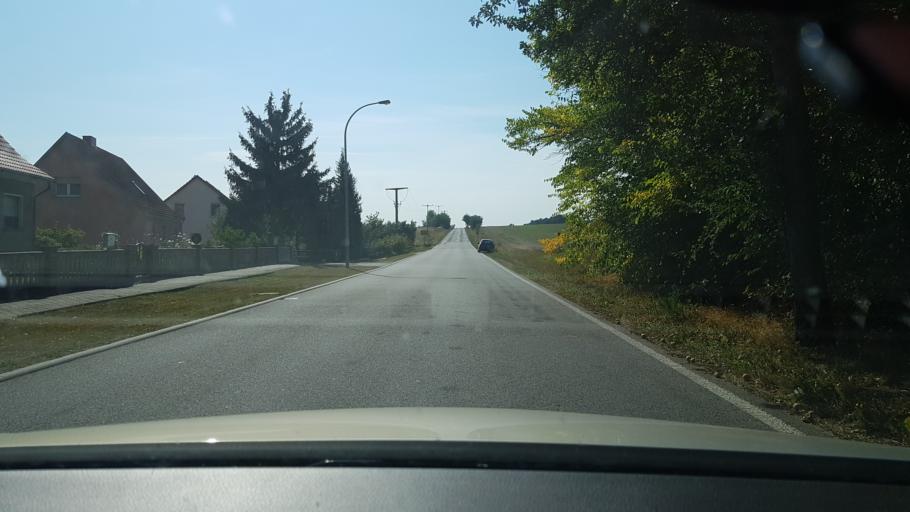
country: DE
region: Brandenburg
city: Lawitz
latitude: 52.1241
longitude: 14.5901
